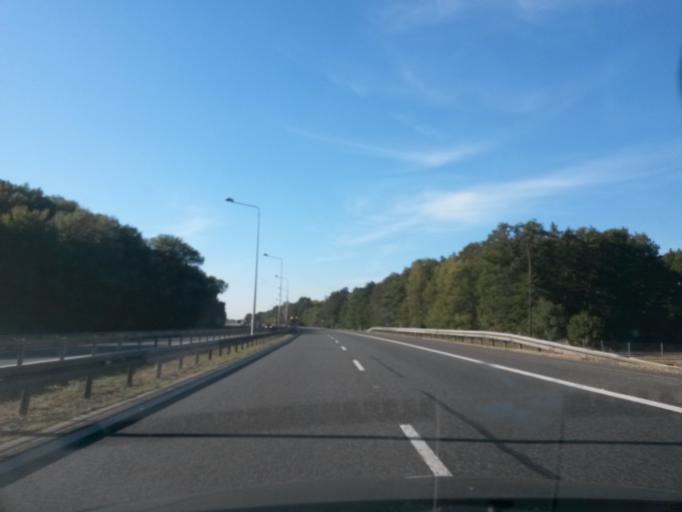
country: PL
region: Opole Voivodeship
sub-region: Powiat brzeski
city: Grodkow
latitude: 50.7663
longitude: 17.4107
